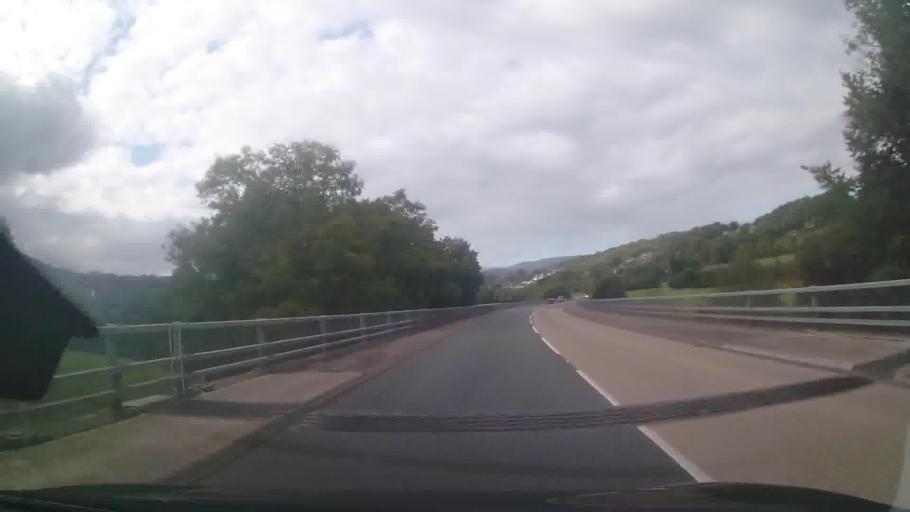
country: GB
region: Wales
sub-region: Gwynedd
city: Dolgellau
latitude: 52.7440
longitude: -3.8694
